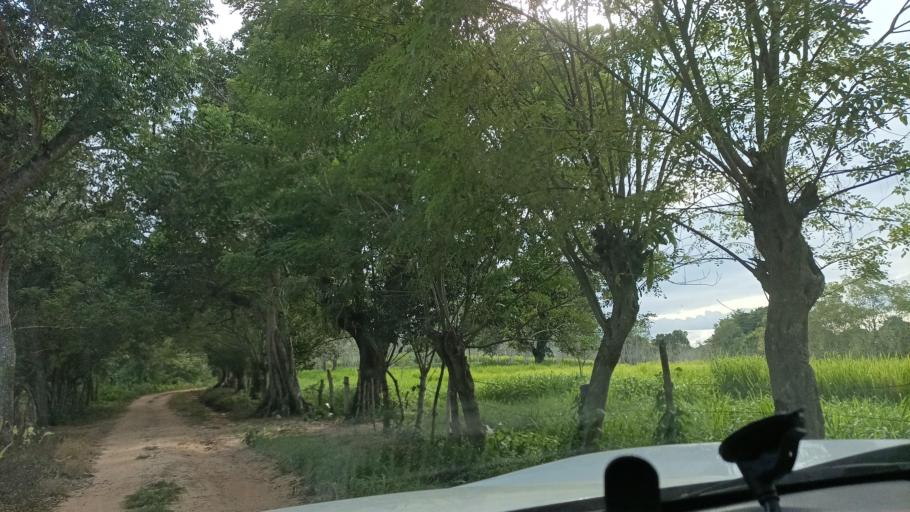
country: MX
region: Veracruz
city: Soconusco
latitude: 17.9496
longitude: -94.8817
